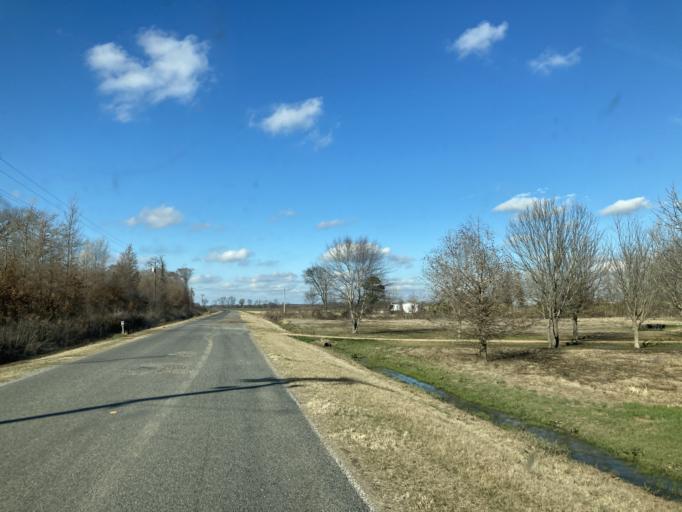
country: US
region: Mississippi
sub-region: Yazoo County
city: Yazoo City
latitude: 32.9321
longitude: -90.4728
